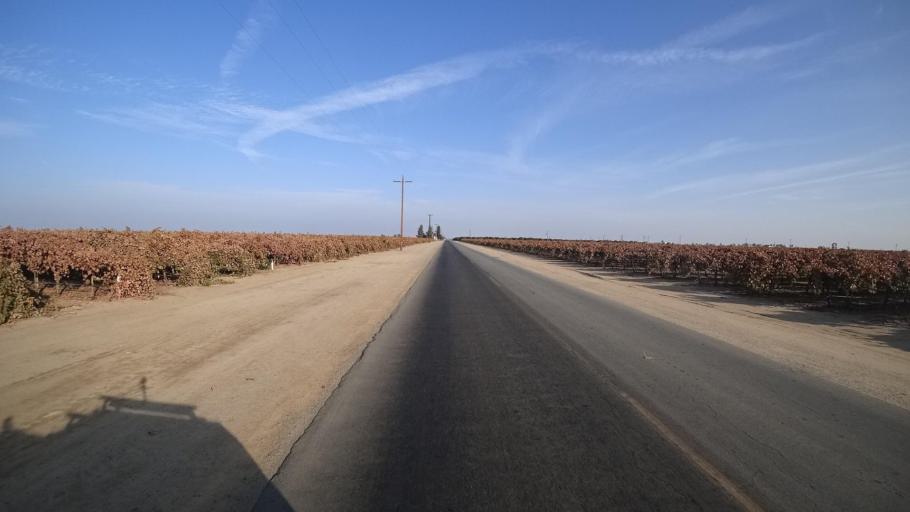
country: US
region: California
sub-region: Kern County
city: Delano
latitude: 35.7550
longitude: -119.1874
